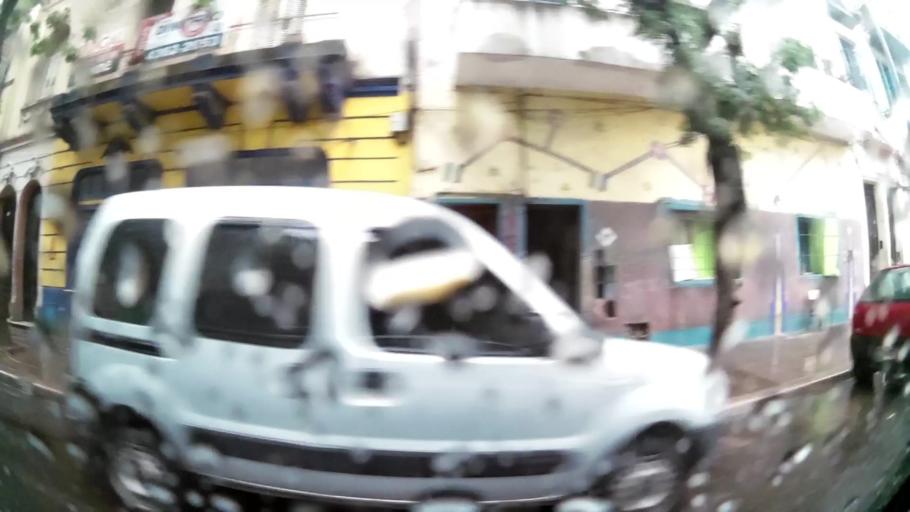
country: AR
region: Buenos Aires
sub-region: Partido de Avellaneda
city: Avellaneda
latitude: -34.6365
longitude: -58.3636
